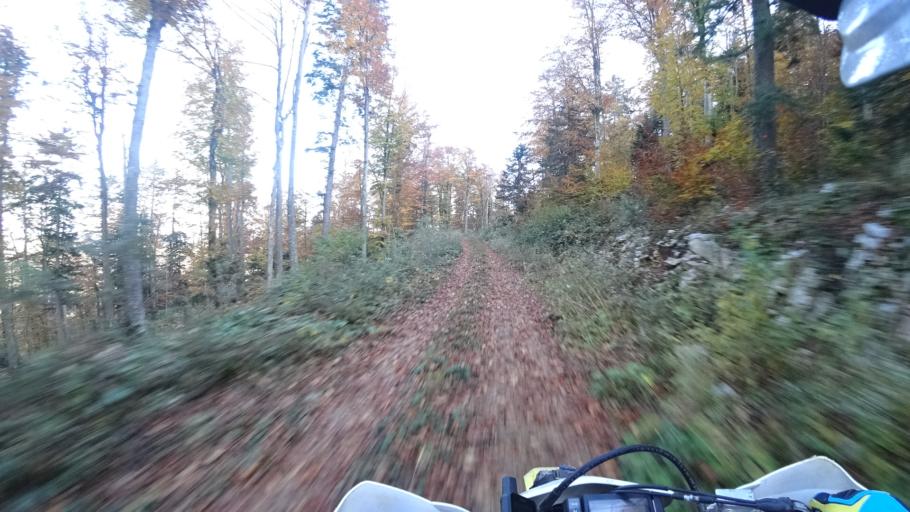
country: HR
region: Karlovacka
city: Plaski
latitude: 44.9590
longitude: 15.4032
